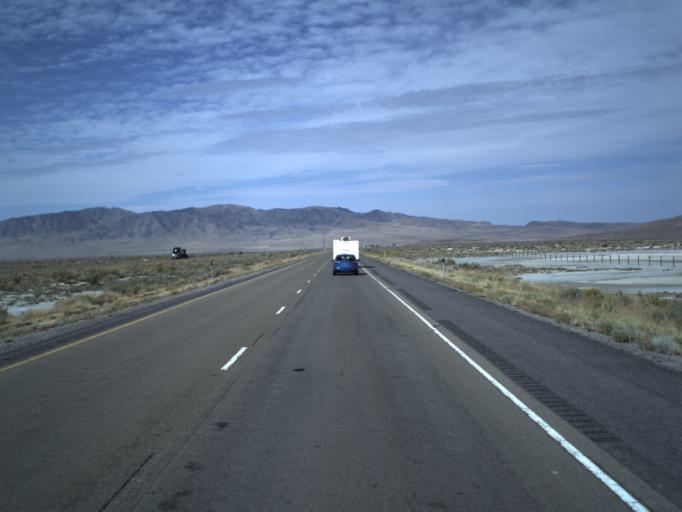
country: US
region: Utah
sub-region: Tooele County
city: Grantsville
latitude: 40.7542
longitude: -112.7333
